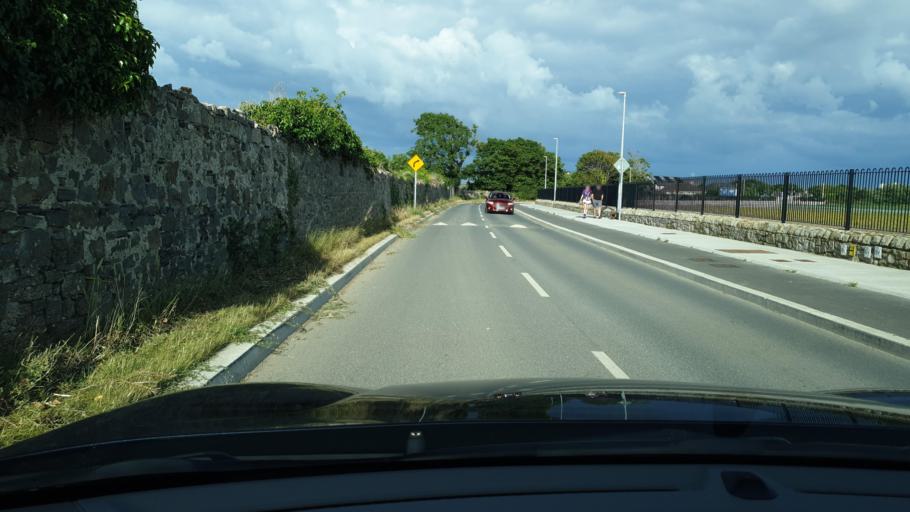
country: IE
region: Leinster
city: An Ros
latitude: 53.5317
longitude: -6.1052
